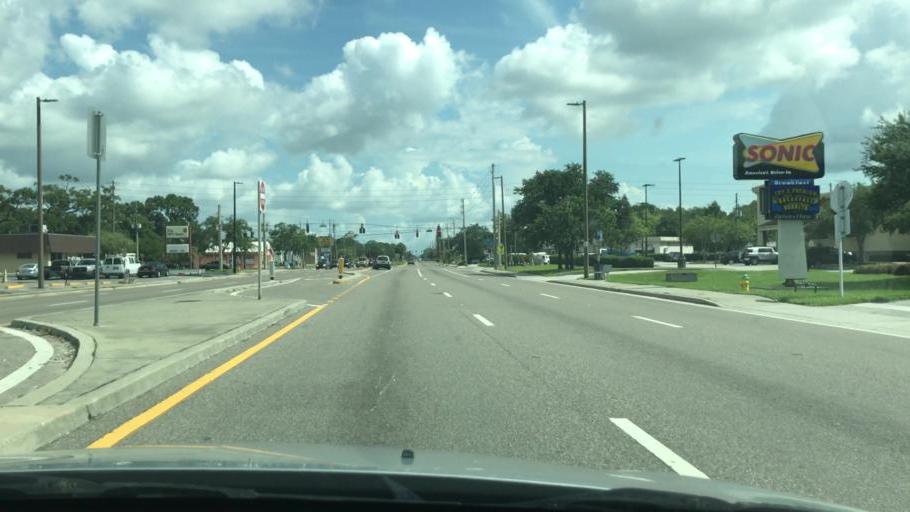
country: US
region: Florida
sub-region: Pinellas County
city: Pinellas Park
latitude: 27.8417
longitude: -82.7000
